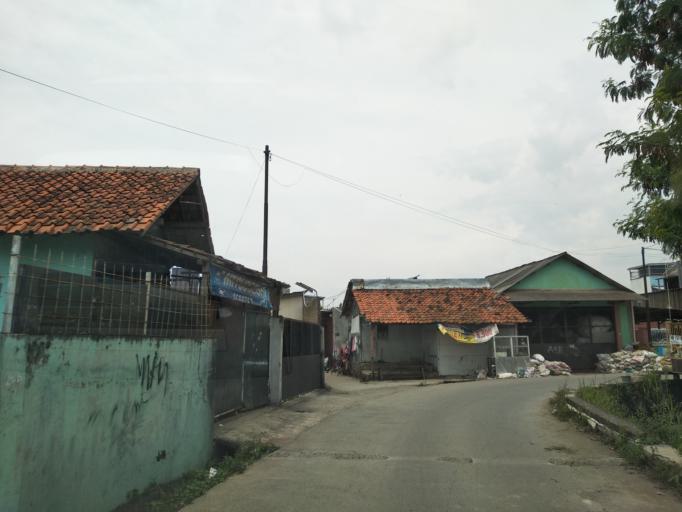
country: ID
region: West Java
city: Pameungpeuk
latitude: -6.9767
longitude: 107.6499
